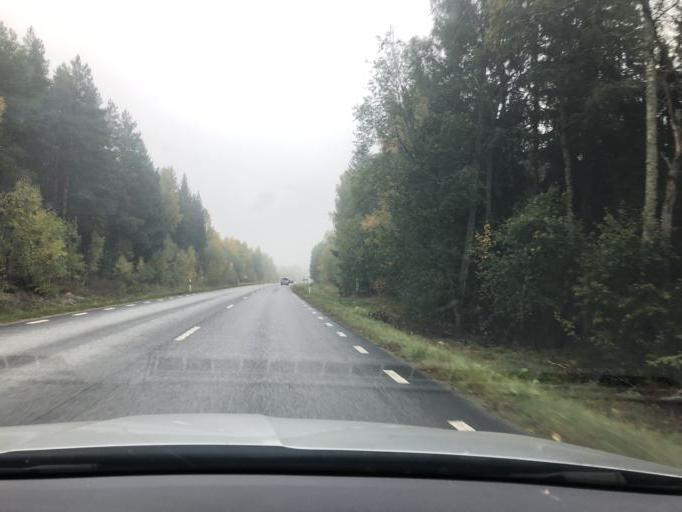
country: SE
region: Uppsala
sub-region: Tierps Kommun
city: Tierp
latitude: 60.3147
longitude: 17.5428
